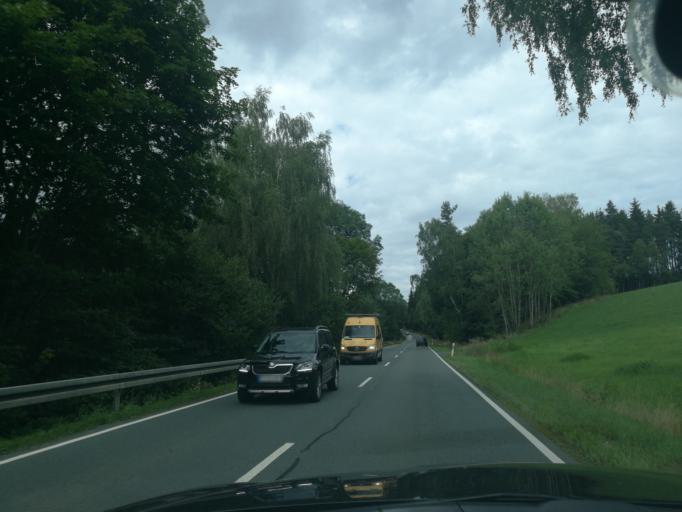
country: DE
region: Saxony
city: Adorf
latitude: 50.3578
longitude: 12.2262
